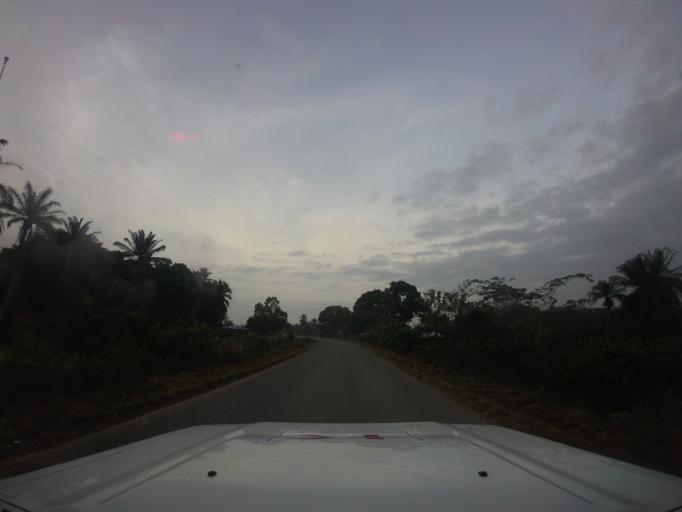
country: LR
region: Bomi
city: Tubmanburg
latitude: 6.7863
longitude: -10.8447
